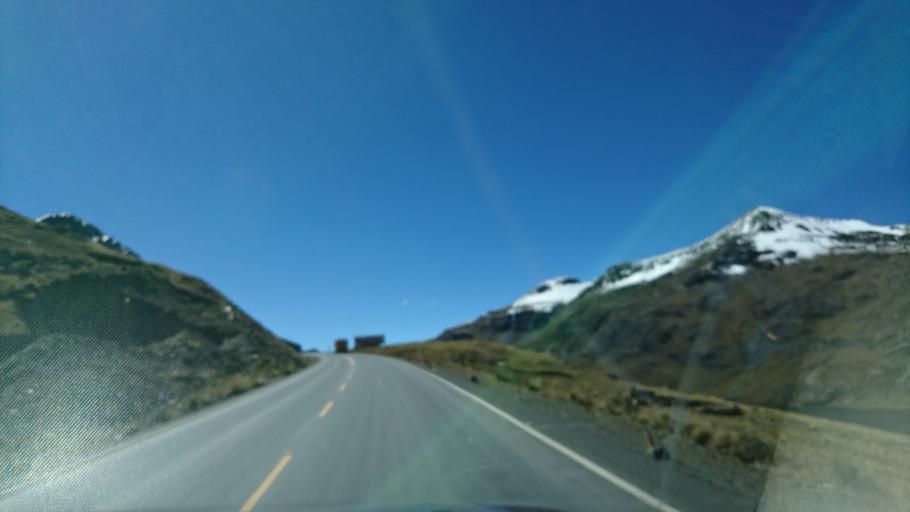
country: BO
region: La Paz
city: La Paz
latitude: -16.3978
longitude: -68.0449
